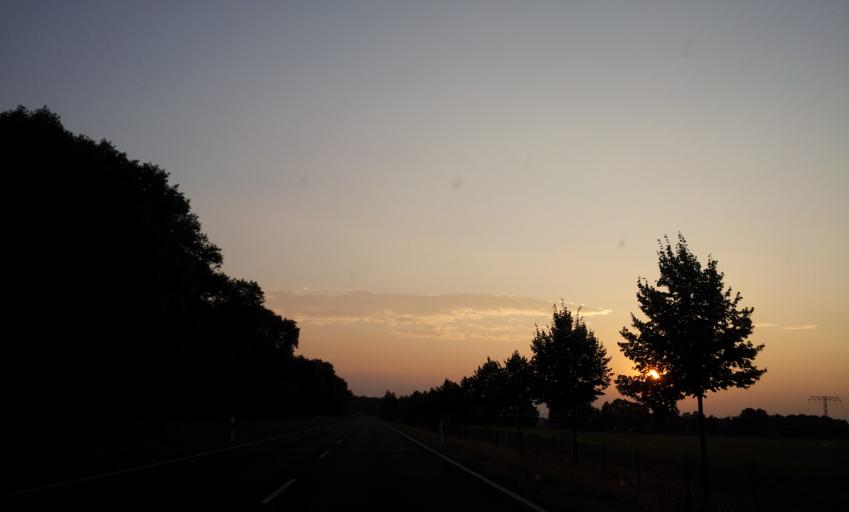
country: DE
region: Brandenburg
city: Luckenwalde
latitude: 52.0974
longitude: 13.1106
